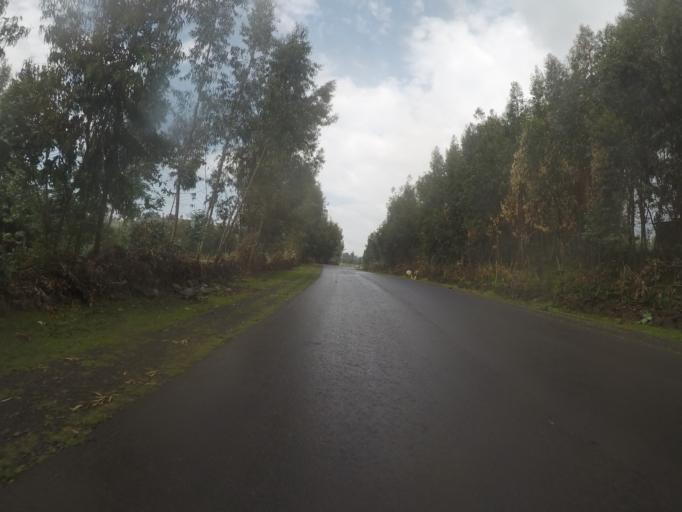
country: ET
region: Amhara
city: Debark'
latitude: 13.1103
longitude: 37.8644
